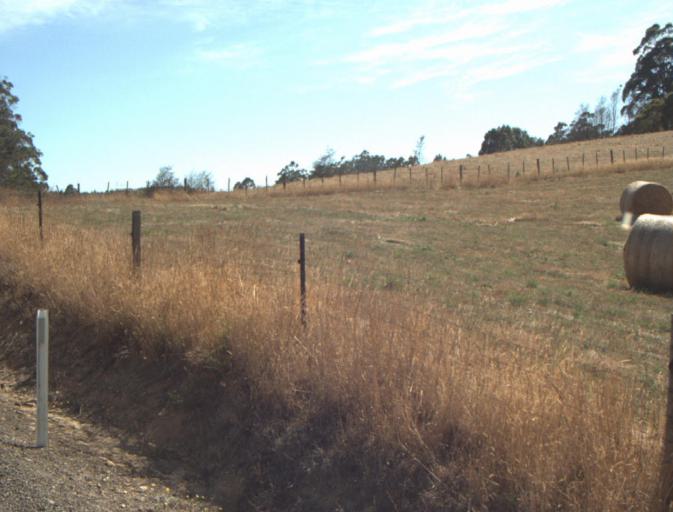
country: AU
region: Tasmania
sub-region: Launceston
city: Mayfield
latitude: -41.2229
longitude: 147.2388
